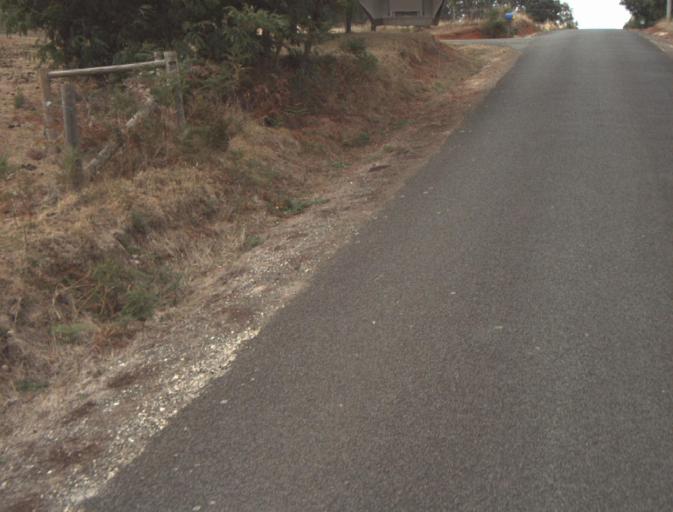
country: AU
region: Tasmania
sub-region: Launceston
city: Mayfield
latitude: -41.2802
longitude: 147.1934
